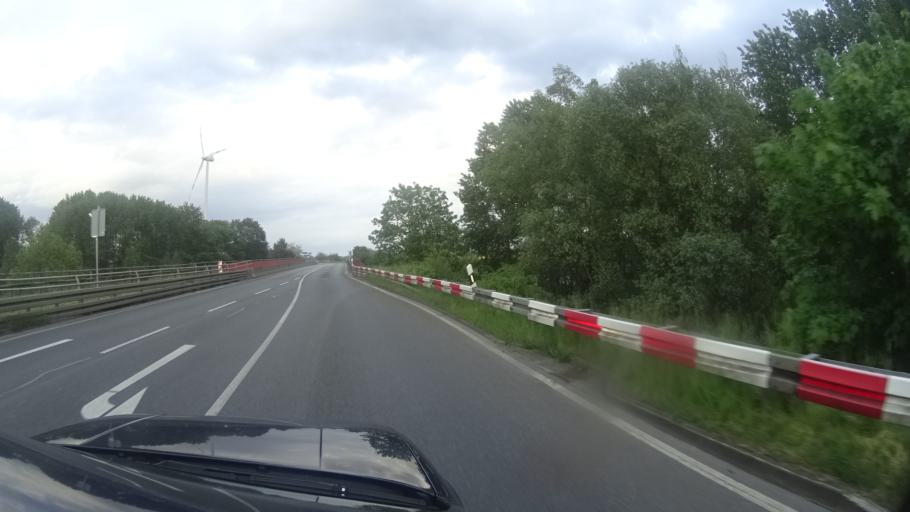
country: DE
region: Brandenburg
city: Dabergotz
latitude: 52.9056
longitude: 12.7373
